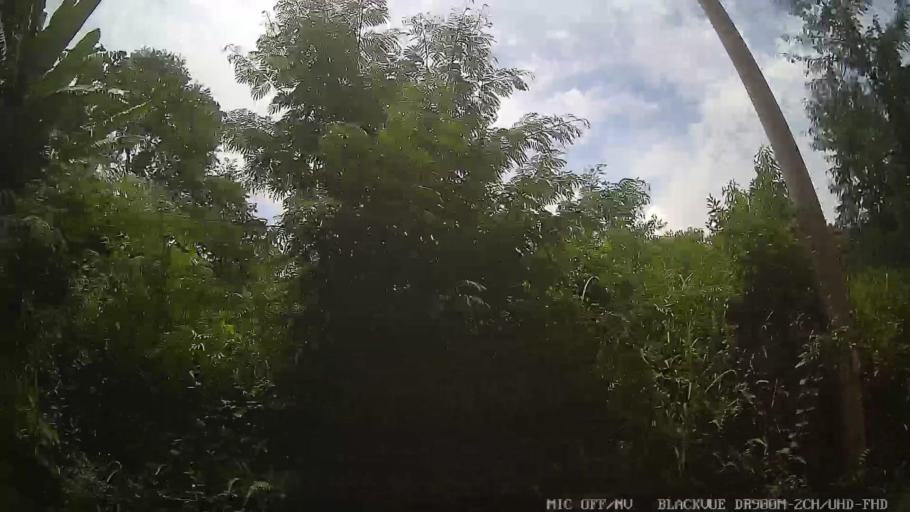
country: BR
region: Sao Paulo
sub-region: Santa Isabel
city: Santa Isabel
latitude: -23.3630
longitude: -46.2296
